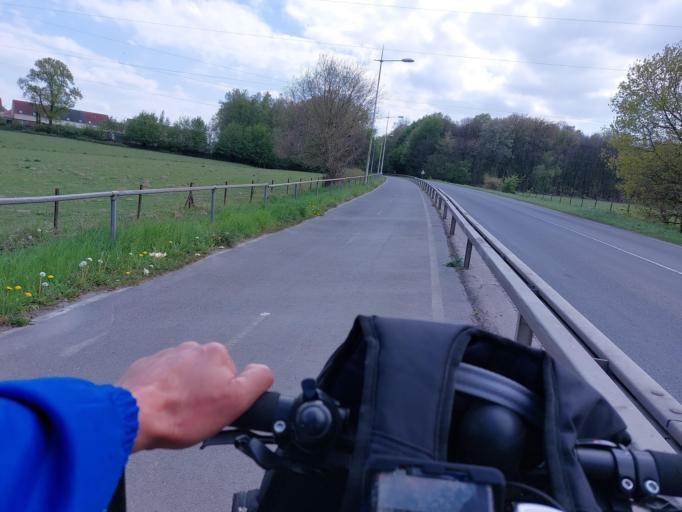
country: FR
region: Nord-Pas-de-Calais
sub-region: Departement du Nord
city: Hautmont
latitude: 50.2591
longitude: 3.8962
